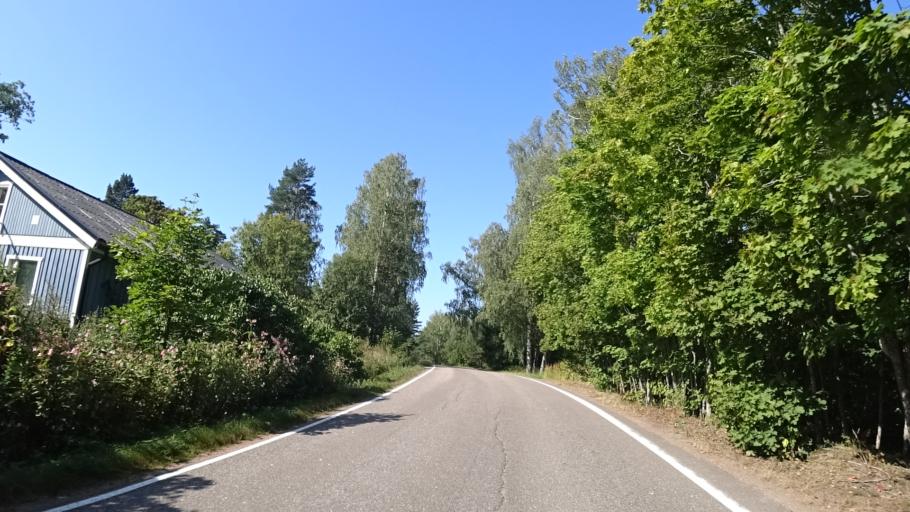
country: FI
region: Kymenlaakso
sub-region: Kotka-Hamina
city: Hamina
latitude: 60.5205
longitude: 27.3373
